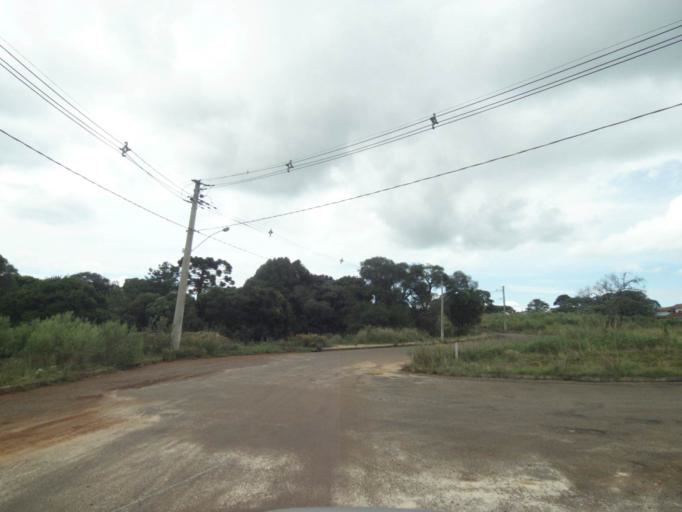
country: BR
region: Rio Grande do Sul
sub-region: Lagoa Vermelha
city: Lagoa Vermelha
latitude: -28.2195
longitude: -51.5186
